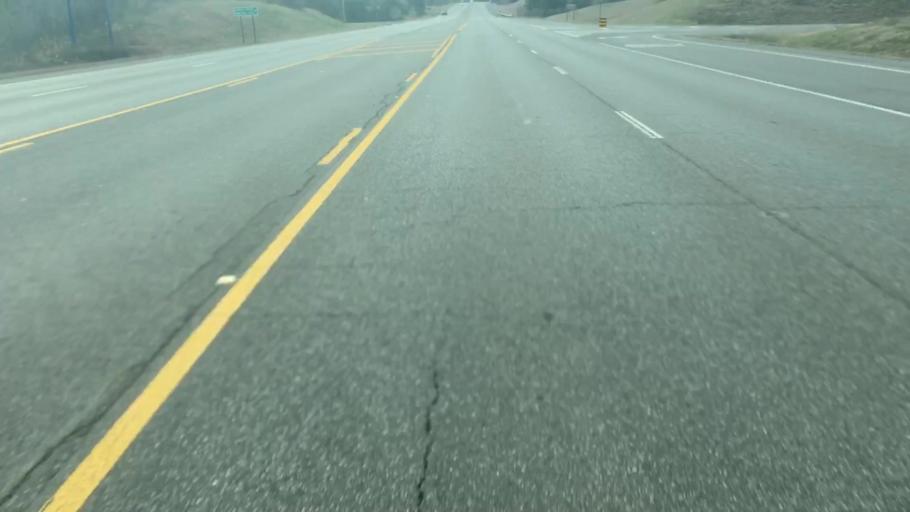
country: US
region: Alabama
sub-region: Walker County
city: Jasper
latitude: 33.8085
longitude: -87.2344
